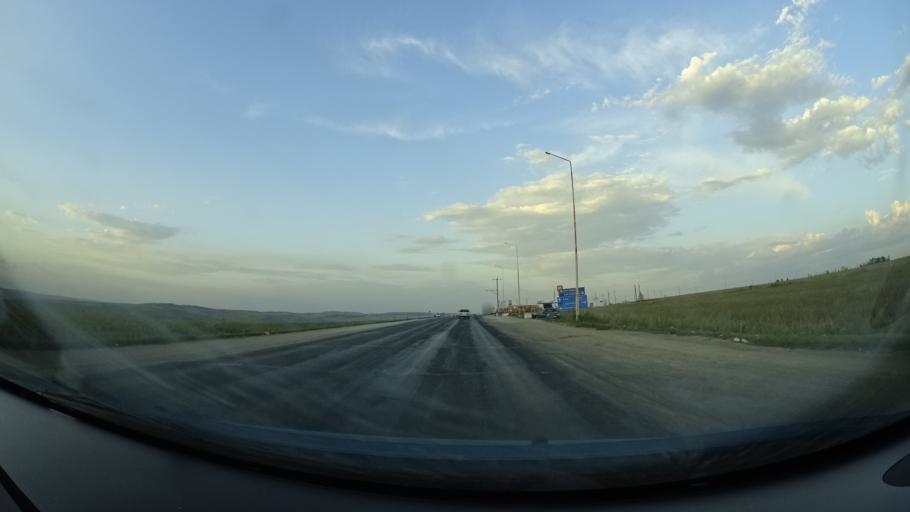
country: RU
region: Orenburg
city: Severnoye
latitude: 54.1142
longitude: 52.5190
